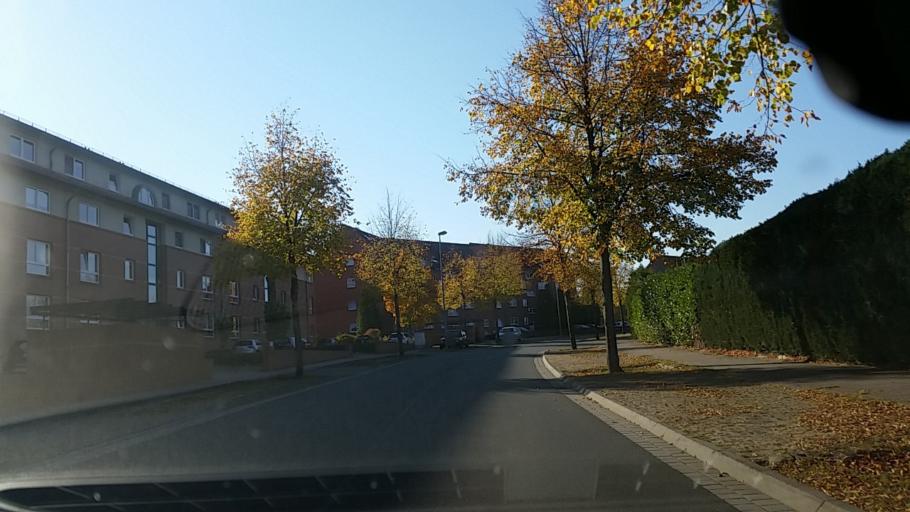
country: DE
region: Lower Saxony
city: Wolfsburg
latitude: 52.4141
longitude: 10.8365
